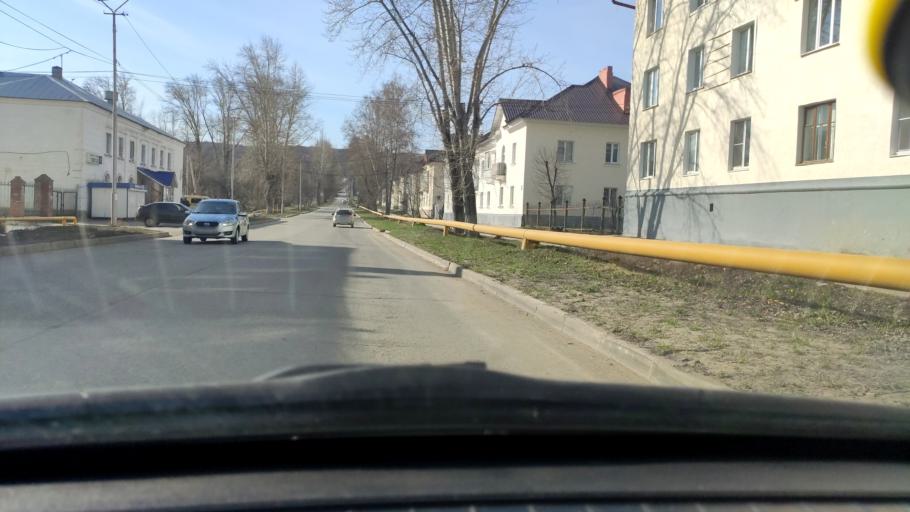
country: RU
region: Samara
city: Zhigulevsk
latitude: 53.4012
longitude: 49.4976
